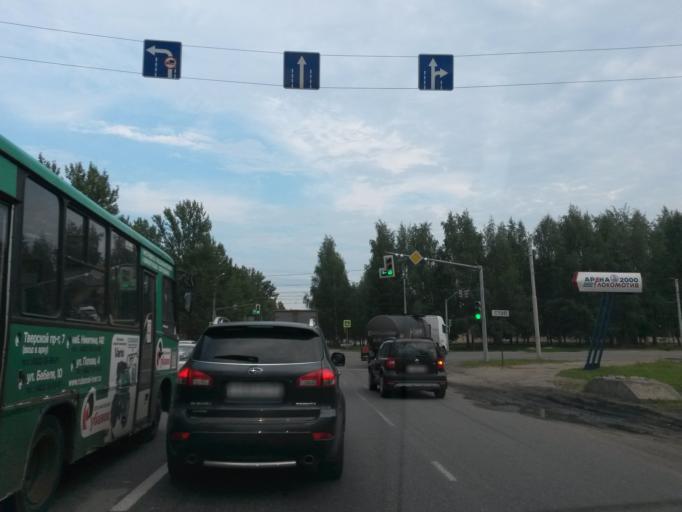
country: RU
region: Jaroslavl
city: Yaroslavl
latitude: 57.5801
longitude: 39.8329
